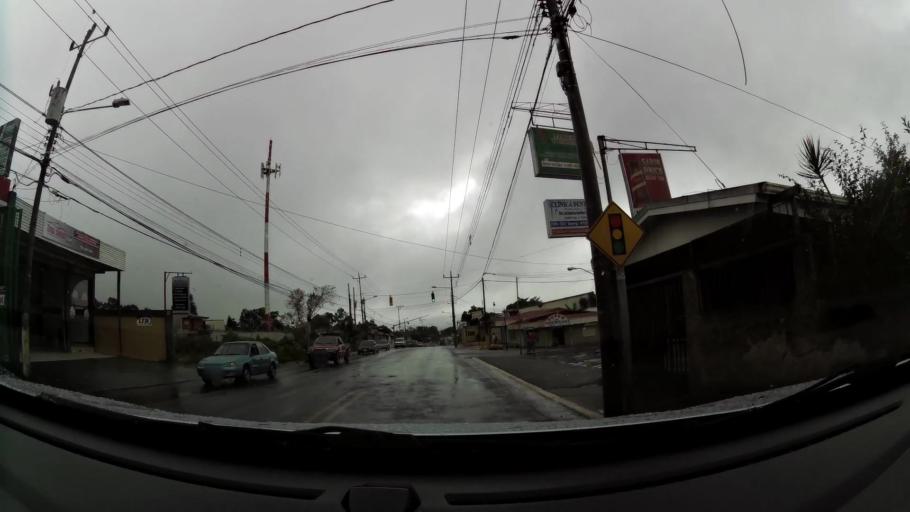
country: CR
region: Cartago
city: Cartago
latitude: 9.8540
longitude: -83.9026
